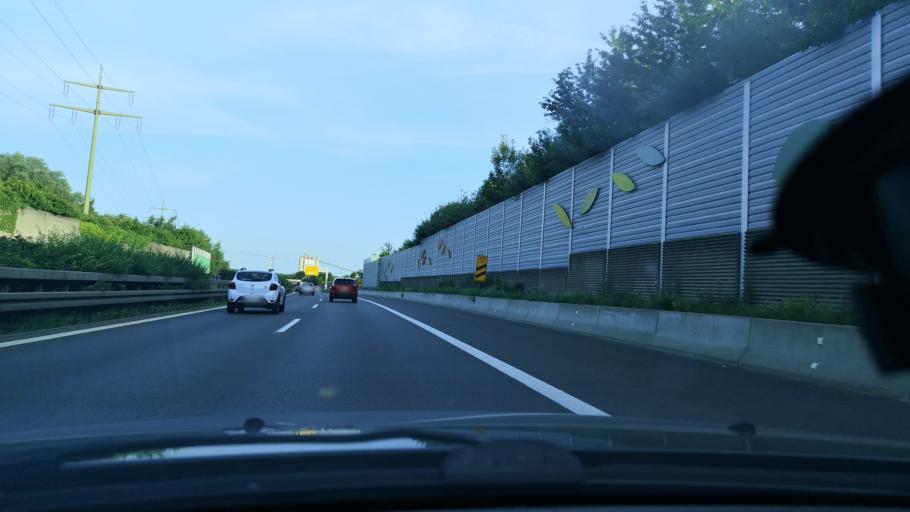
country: DE
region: Baden-Wuerttemberg
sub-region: Regierungsbezirk Stuttgart
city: Eislingen
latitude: 48.6915
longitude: 9.6908
